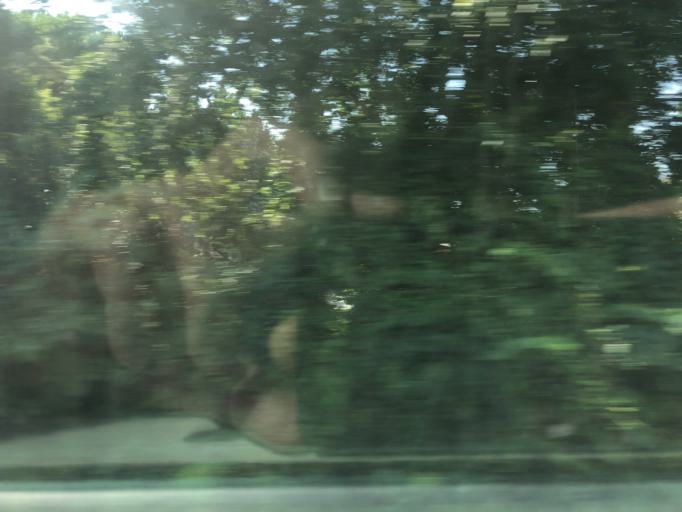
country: IT
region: Emilia-Romagna
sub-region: Provincia di Rimini
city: Rimini
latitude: 44.0708
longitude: 12.5473
